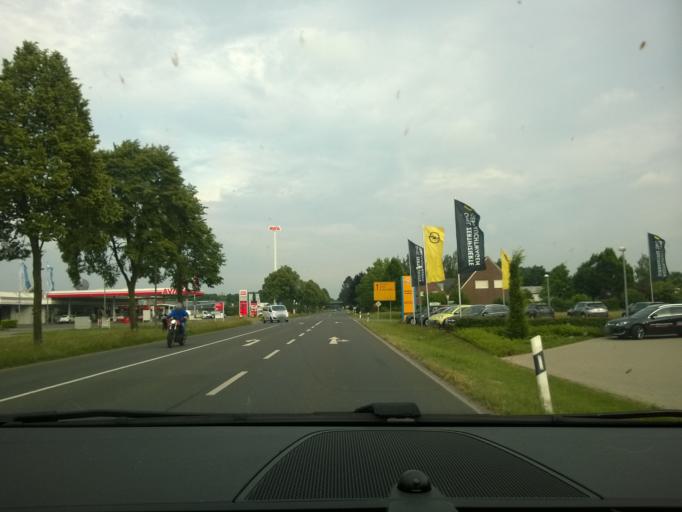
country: DE
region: North Rhine-Westphalia
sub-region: Regierungsbezirk Munster
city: Gescher
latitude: 51.9428
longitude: 7.0242
